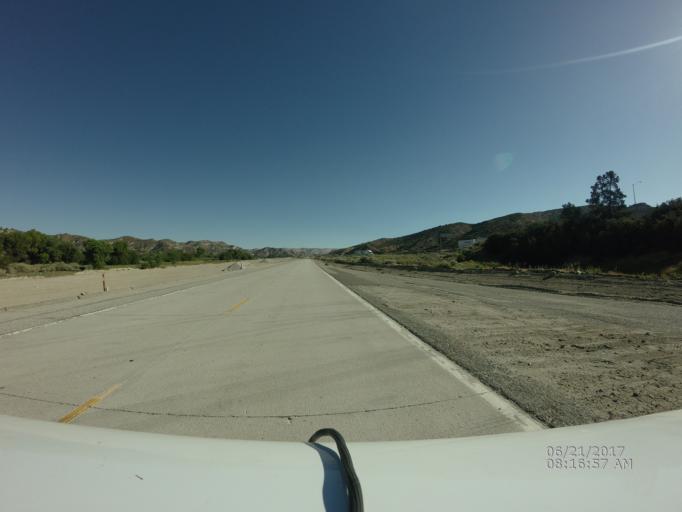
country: US
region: California
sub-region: Kern County
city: Lebec
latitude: 34.7101
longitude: -118.7983
